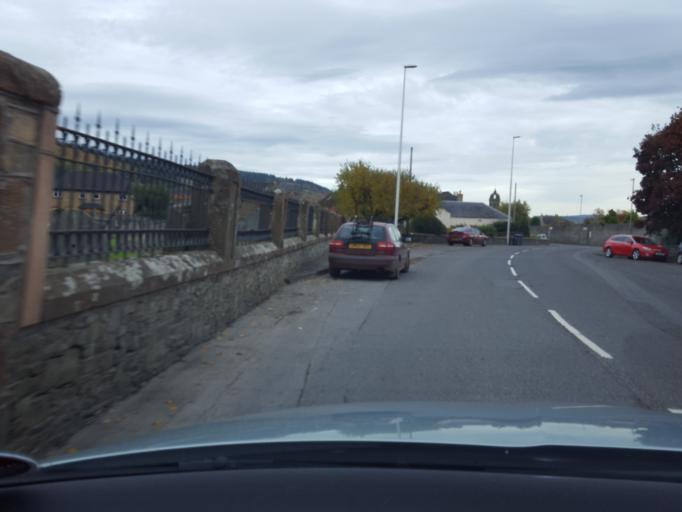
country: GB
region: Scotland
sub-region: The Scottish Borders
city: Peebles
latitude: 55.6526
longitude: -3.2001
